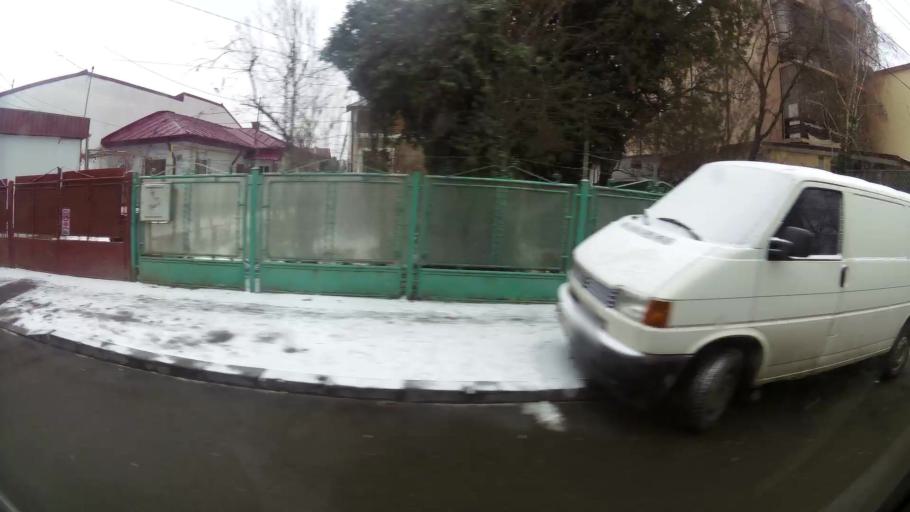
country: RO
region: Prahova
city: Ploiesti
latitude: 44.9389
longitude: 25.9964
